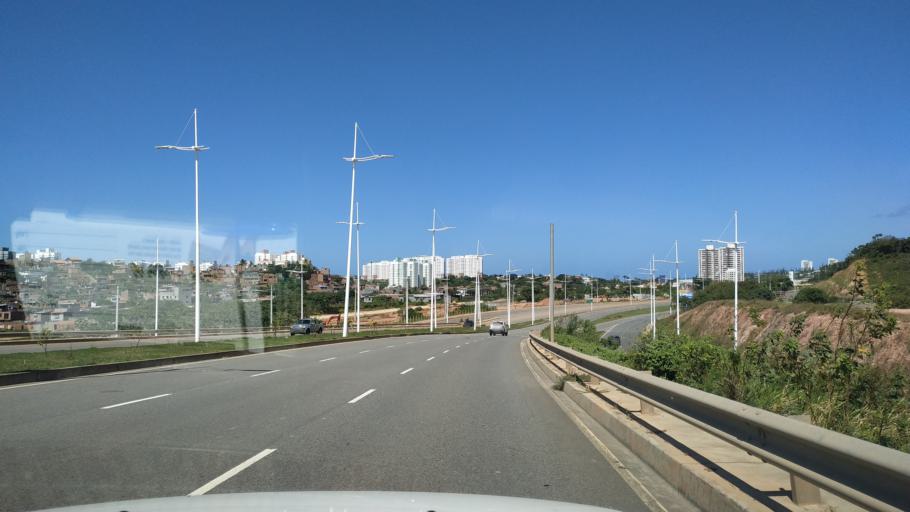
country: BR
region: Bahia
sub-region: Lauro De Freitas
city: Lauro de Freitas
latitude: -12.9283
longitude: -38.3816
